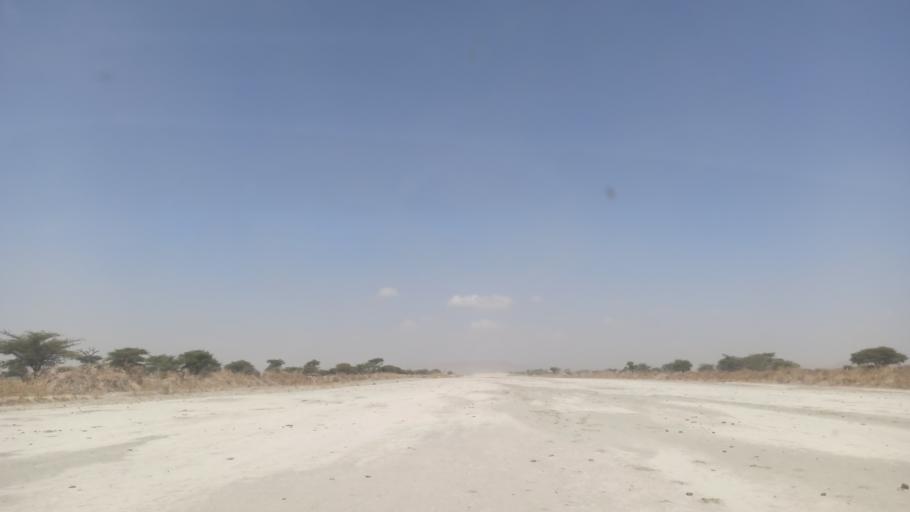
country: ET
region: Oromiya
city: Ziway
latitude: 7.7139
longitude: 38.6344
